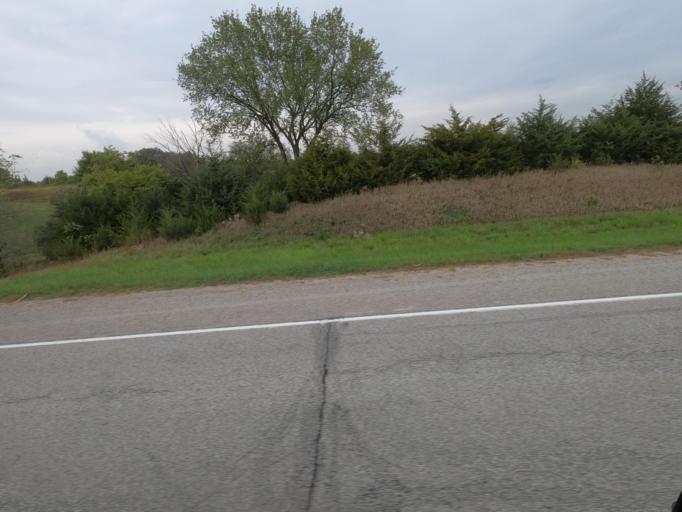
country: US
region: Iowa
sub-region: Van Buren County
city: Keosauqua
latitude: 40.8503
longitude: -92.0463
